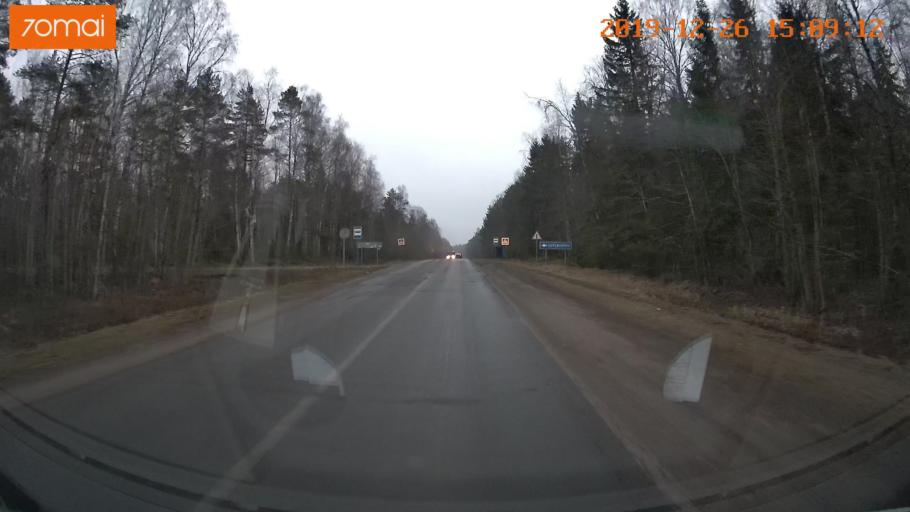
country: RU
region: Jaroslavl
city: Rybinsk
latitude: 58.1513
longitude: 38.8386
